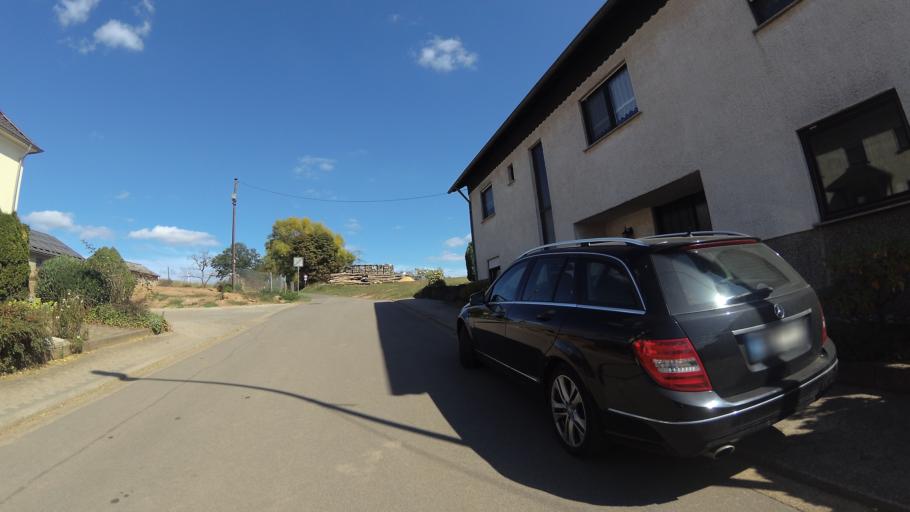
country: DE
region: Saarland
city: Lebach
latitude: 49.4303
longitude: 6.9176
